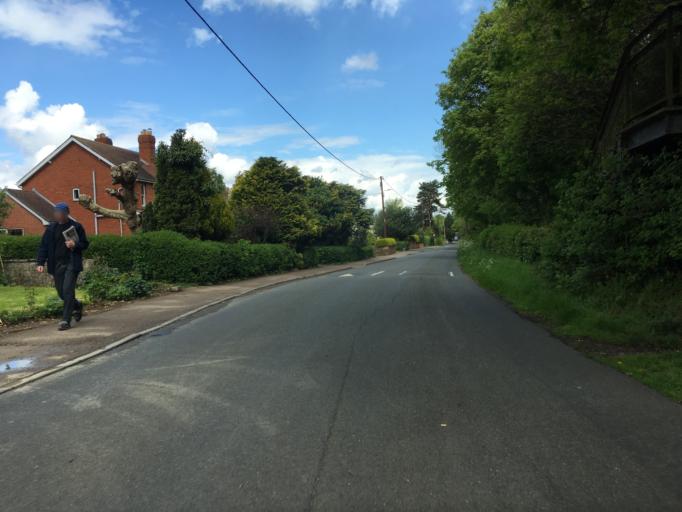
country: GB
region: England
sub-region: Gloucestershire
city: Dursley
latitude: 51.6924
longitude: -2.3560
